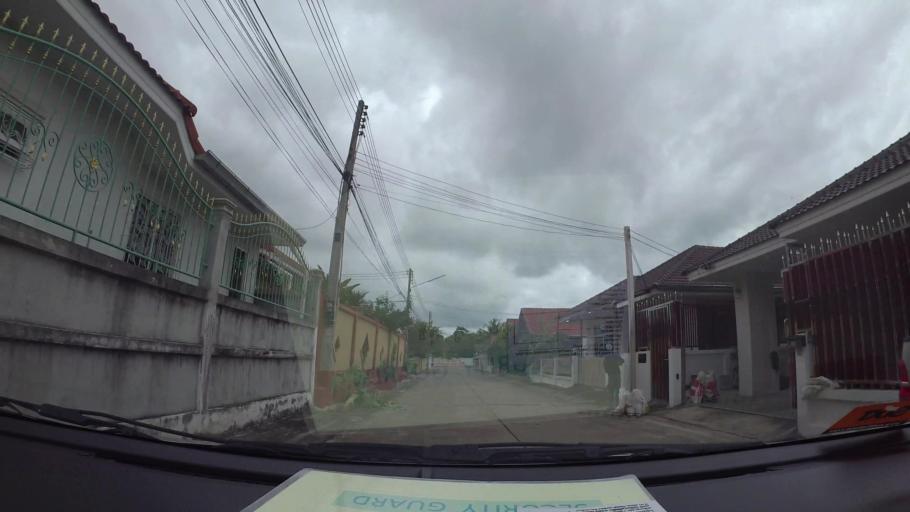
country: TH
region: Chon Buri
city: Sattahip
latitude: 12.7604
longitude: 100.9081
